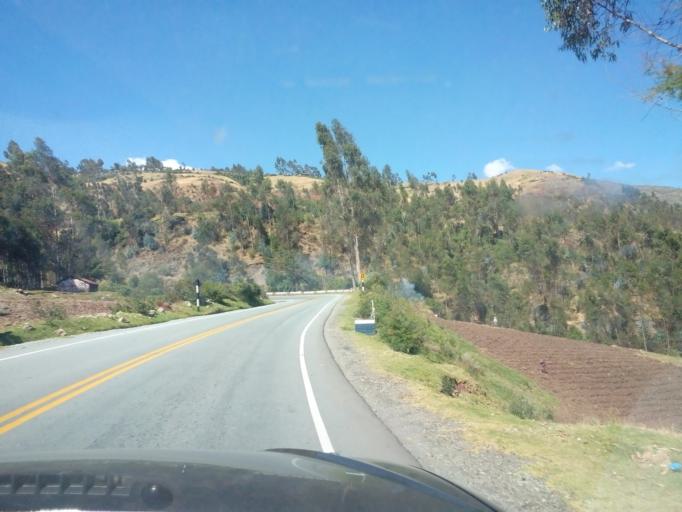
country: PE
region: Cusco
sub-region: Provincia de Anta
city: Limatambo
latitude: -13.4503
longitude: -72.3976
